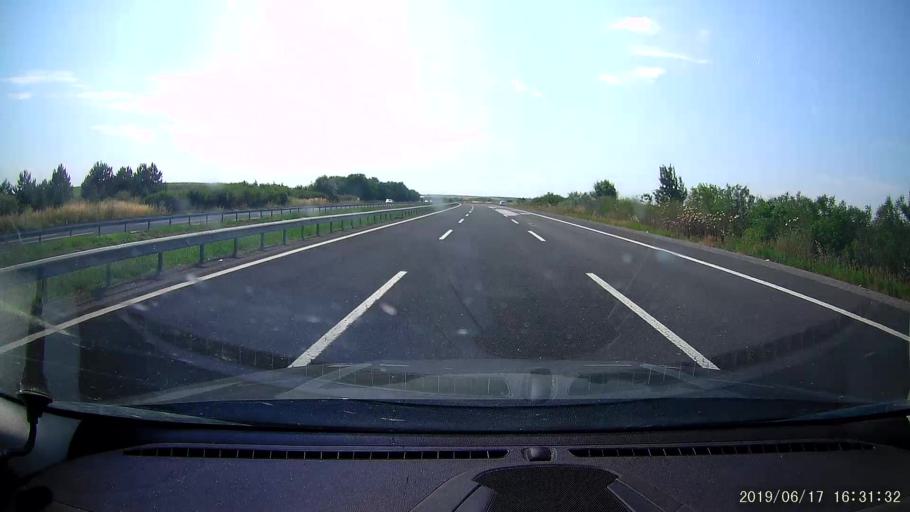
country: TR
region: Tekirdag
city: Beyazkoy
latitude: 41.3626
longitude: 27.6250
